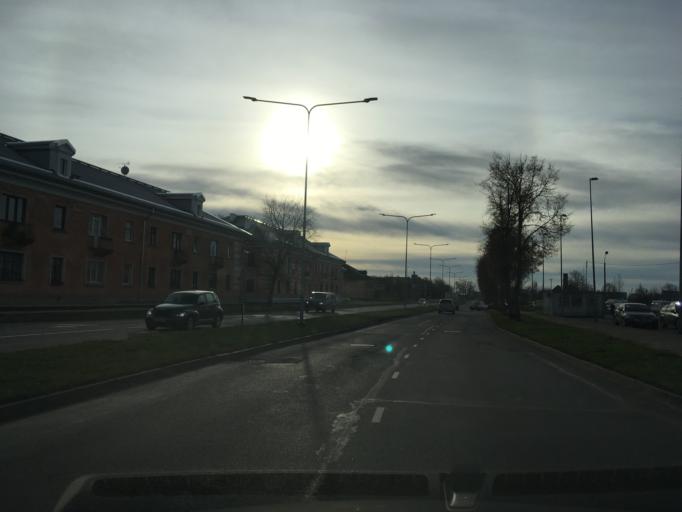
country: EE
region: Ida-Virumaa
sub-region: Narva linn
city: Narva
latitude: 59.3646
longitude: 28.1881
